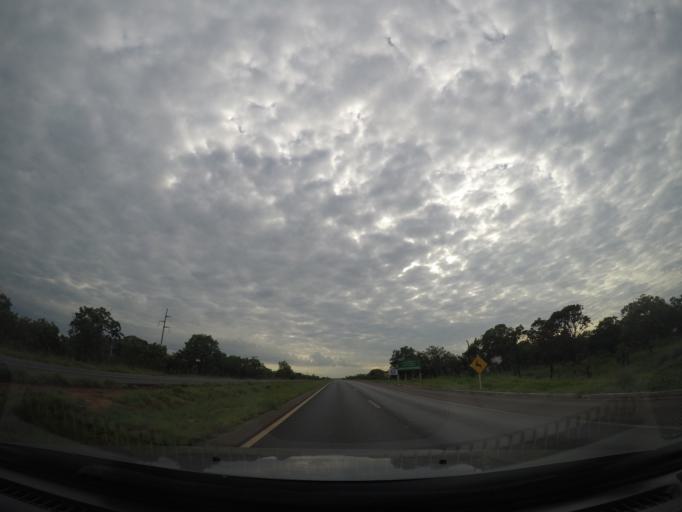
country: BR
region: Goias
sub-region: Planaltina
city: Planaltina
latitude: -15.5965
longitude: -47.6396
